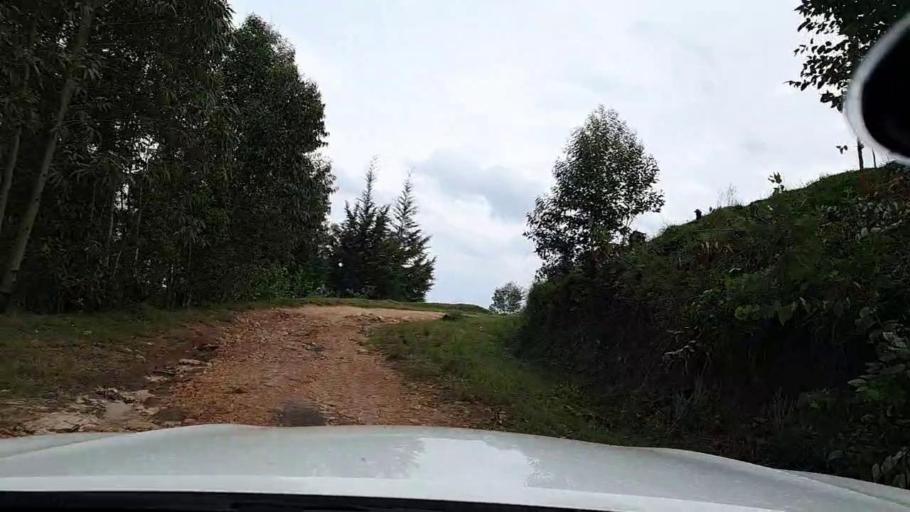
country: RW
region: Western Province
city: Kibuye
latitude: -2.1925
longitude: 29.3167
